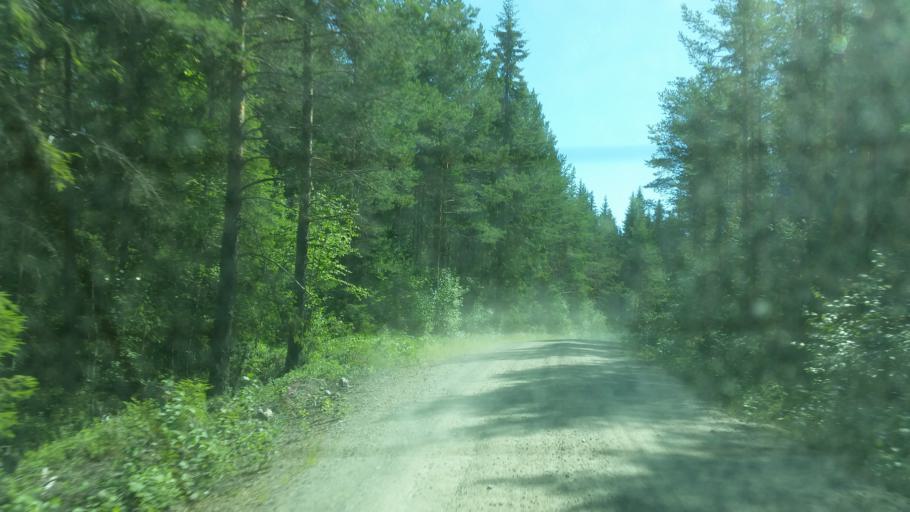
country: SE
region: Vaesternorrland
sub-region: Ange Kommun
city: Ange
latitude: 62.1811
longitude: 15.6227
